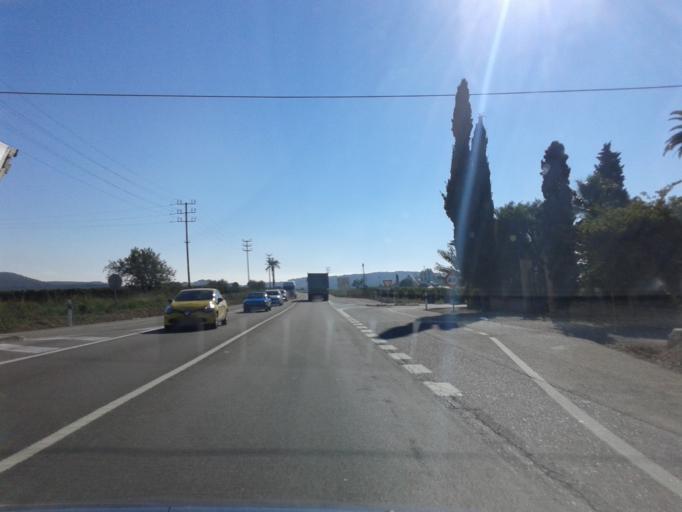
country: ES
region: Catalonia
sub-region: Provincia de Tarragona
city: Santa Oliva
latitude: 41.2496
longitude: 1.5903
